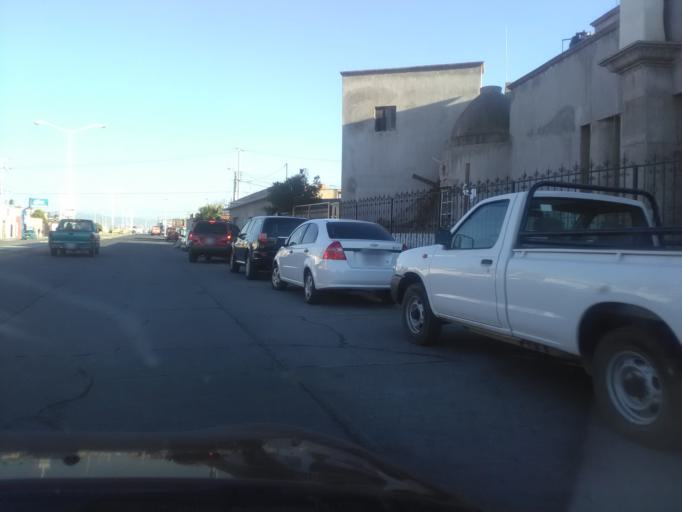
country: MX
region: Durango
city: Victoria de Durango
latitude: 24.0582
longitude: -104.5914
